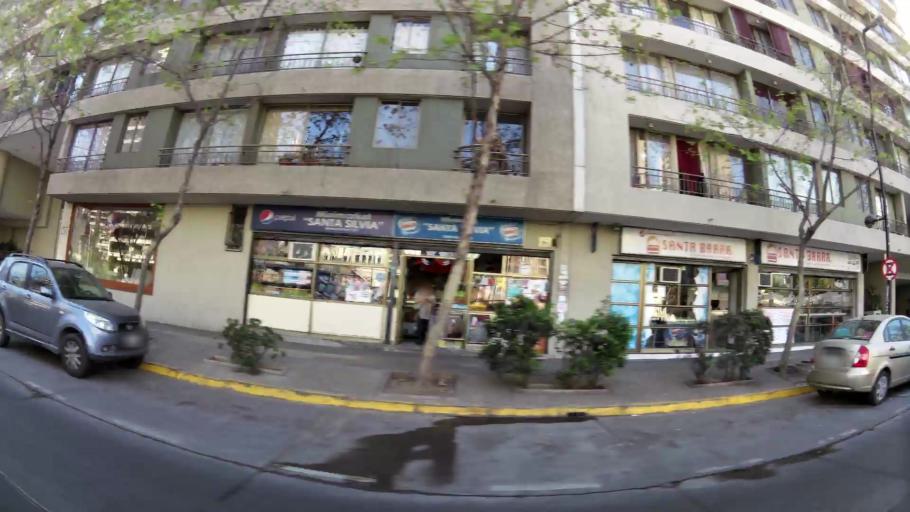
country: CL
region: Santiago Metropolitan
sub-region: Provincia de Santiago
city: Santiago
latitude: -33.4478
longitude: -70.6337
